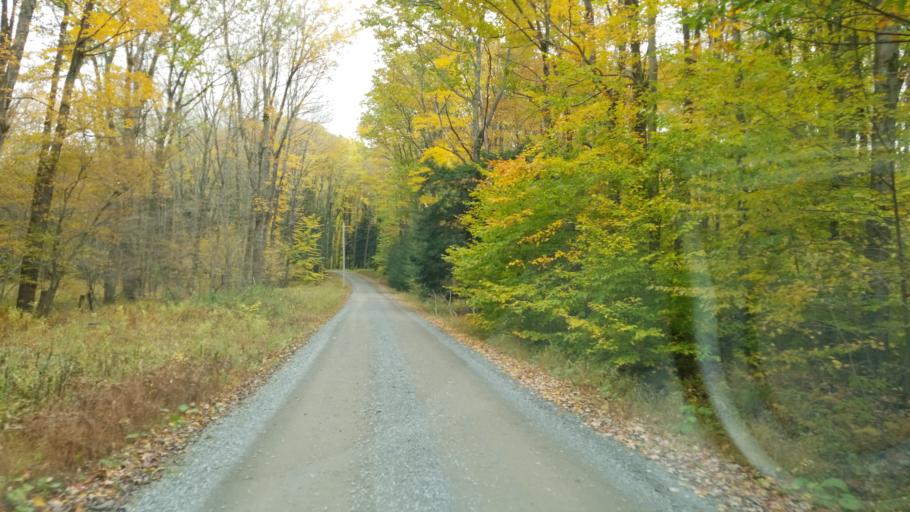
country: US
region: Pennsylvania
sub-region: Clearfield County
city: Clearfield
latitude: 41.1993
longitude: -78.4188
